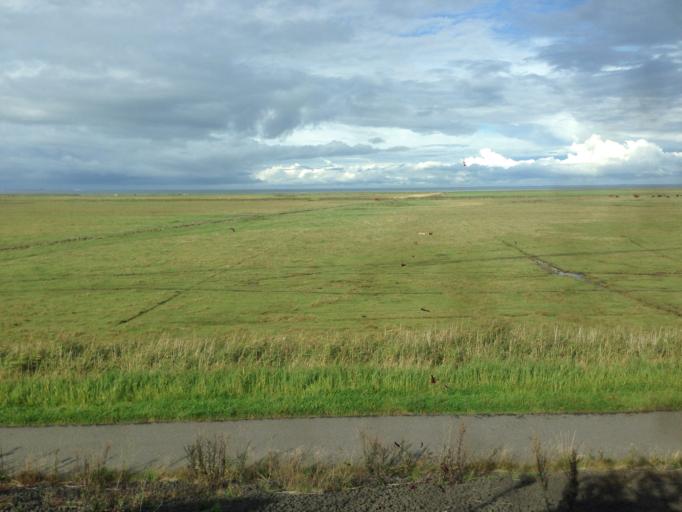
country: DE
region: Schleswig-Holstein
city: Keitum
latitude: 54.8827
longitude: 8.3850
